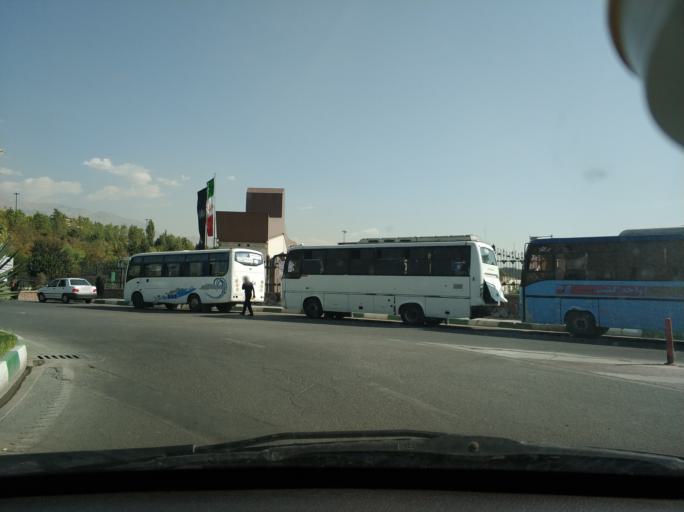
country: IR
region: Tehran
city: Tehran
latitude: 35.7489
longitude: 51.3784
